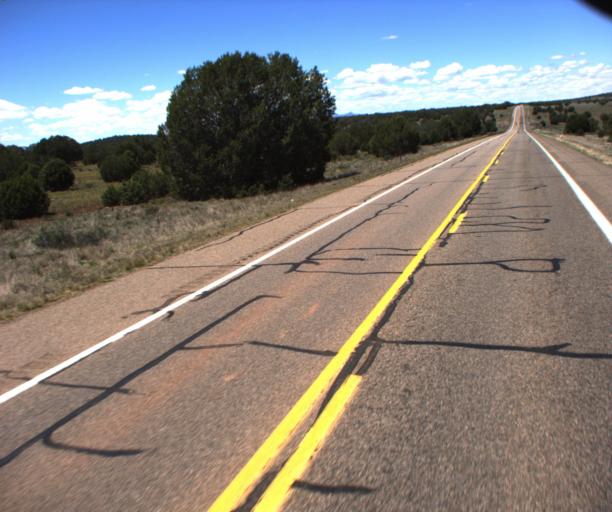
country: US
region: Arizona
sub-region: Yavapai County
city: Paulden
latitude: 35.1386
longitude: -112.4424
